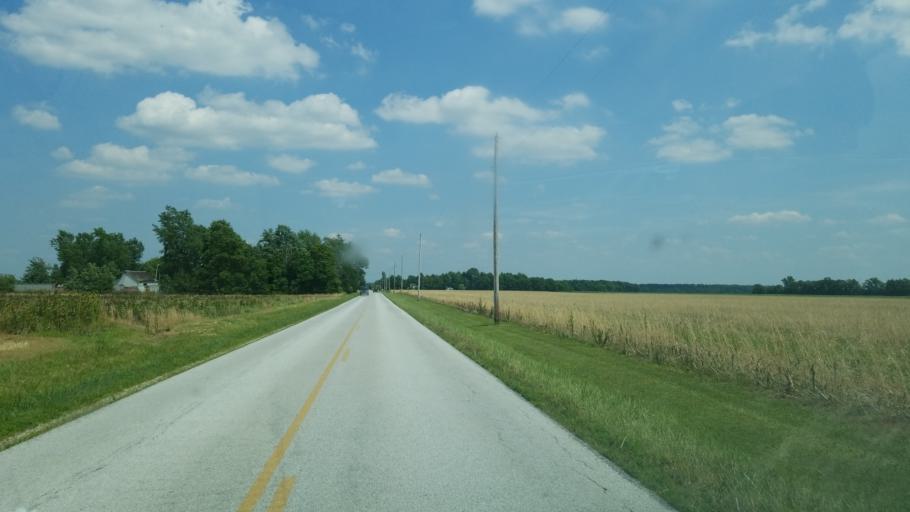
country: US
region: Ohio
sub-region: Seneca County
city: Tiffin
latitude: 41.1666
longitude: -83.2423
